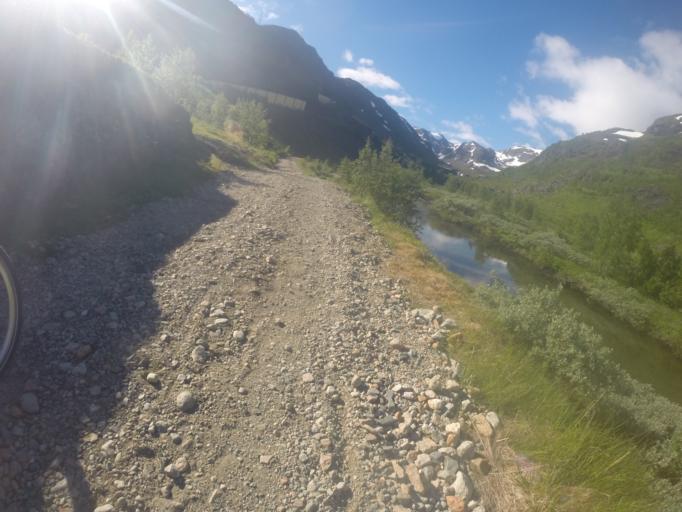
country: NO
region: Sogn og Fjordane
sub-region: Aurland
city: Aurlandsvangen
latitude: 60.7397
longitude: 7.1204
